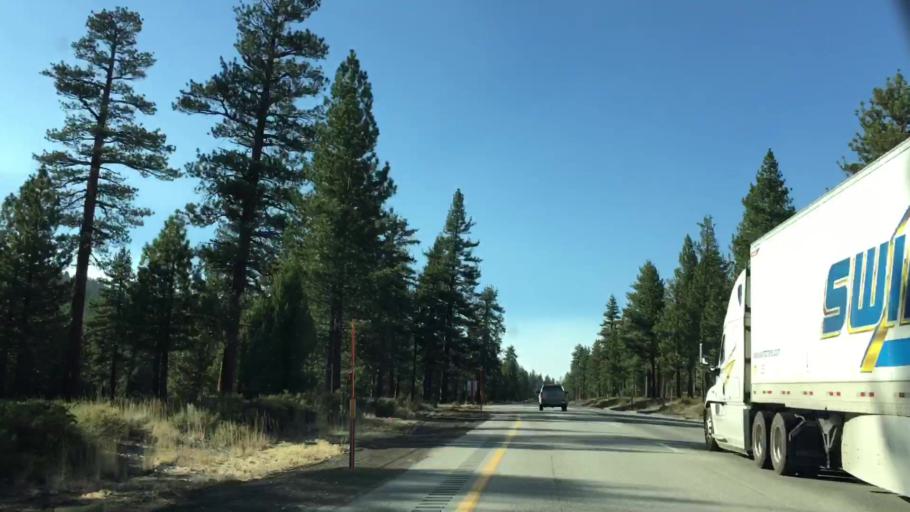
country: US
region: California
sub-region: Mono County
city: Mammoth Lakes
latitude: 37.6706
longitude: -118.9352
